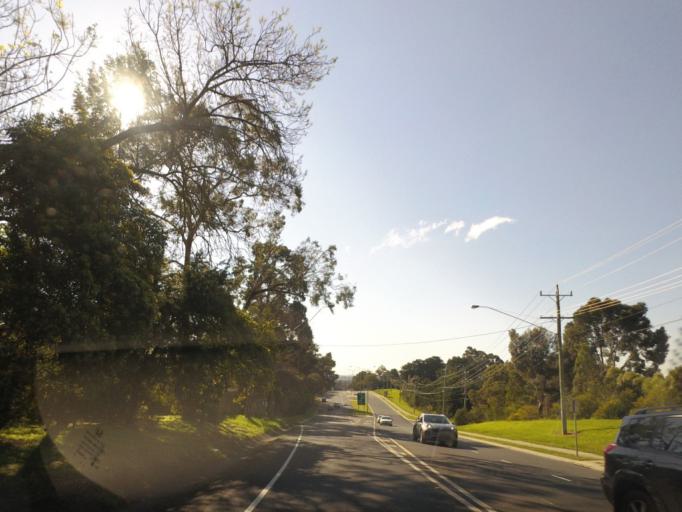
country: AU
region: Victoria
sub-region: Manningham
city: Donvale
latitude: -37.7863
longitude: 145.1810
